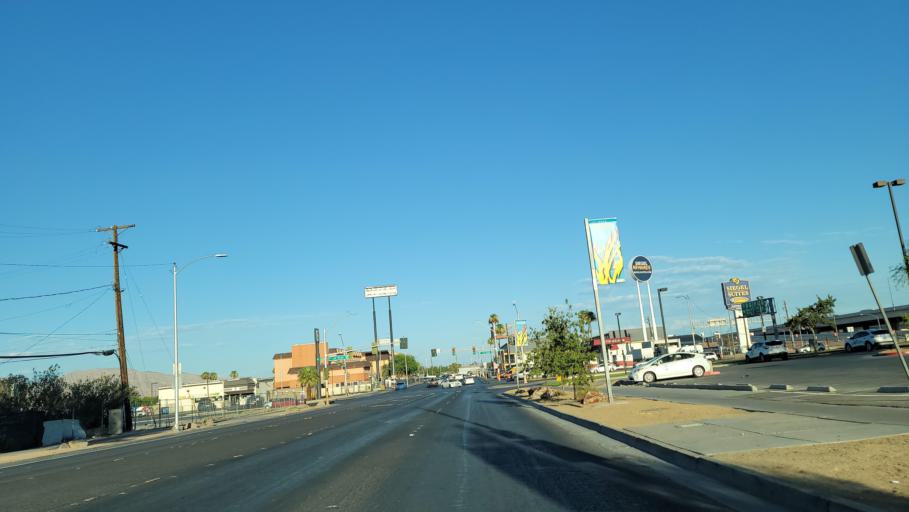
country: US
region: Nevada
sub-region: Clark County
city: Las Vegas
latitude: 36.1753
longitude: -115.1382
